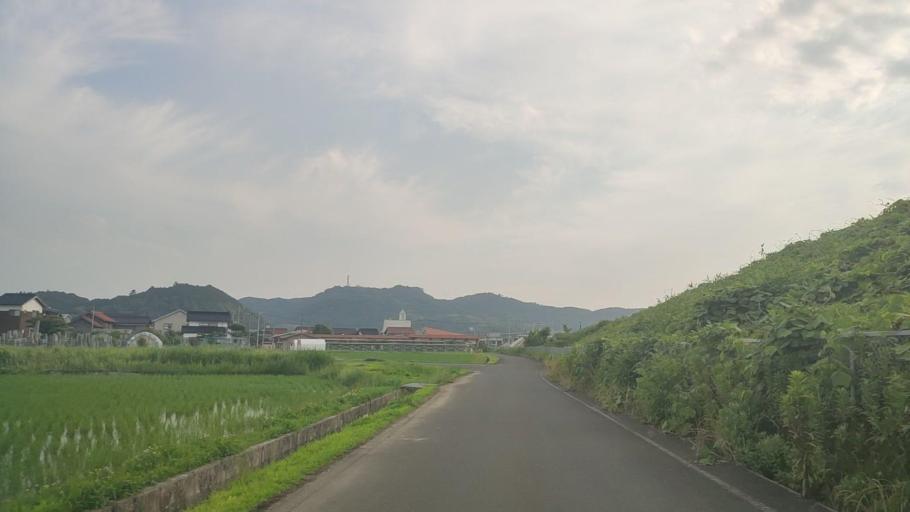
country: JP
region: Tottori
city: Kurayoshi
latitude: 35.4864
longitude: 133.8099
